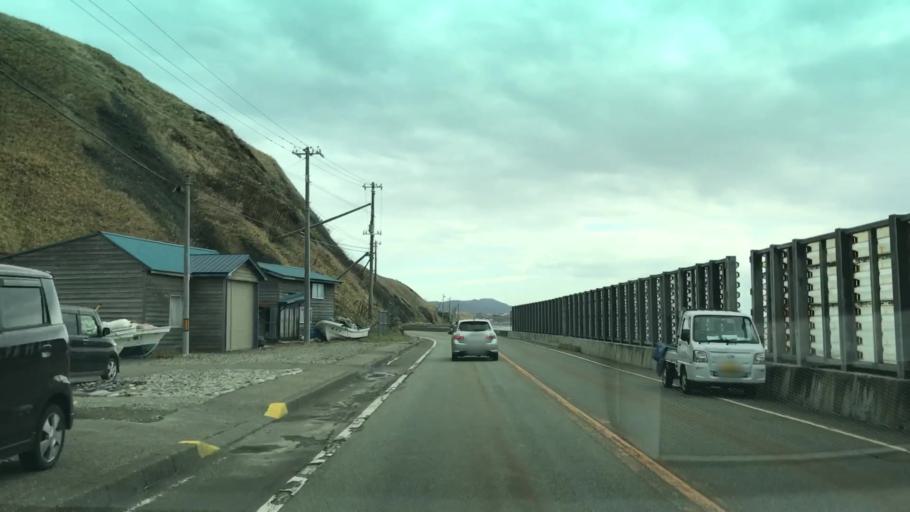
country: JP
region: Hokkaido
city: Shizunai-furukawacho
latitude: 42.0537
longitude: 143.0857
